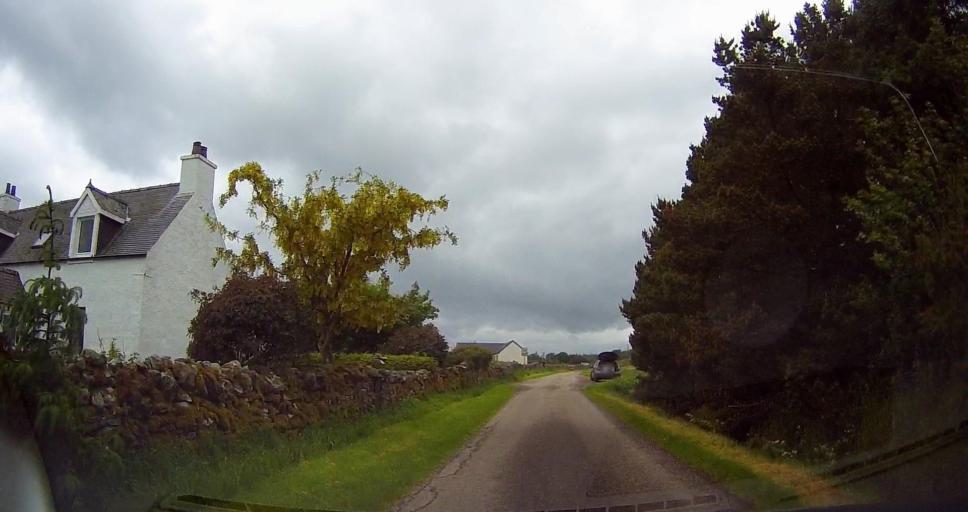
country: GB
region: Scotland
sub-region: Highland
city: Alness
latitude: 58.0764
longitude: -4.4427
